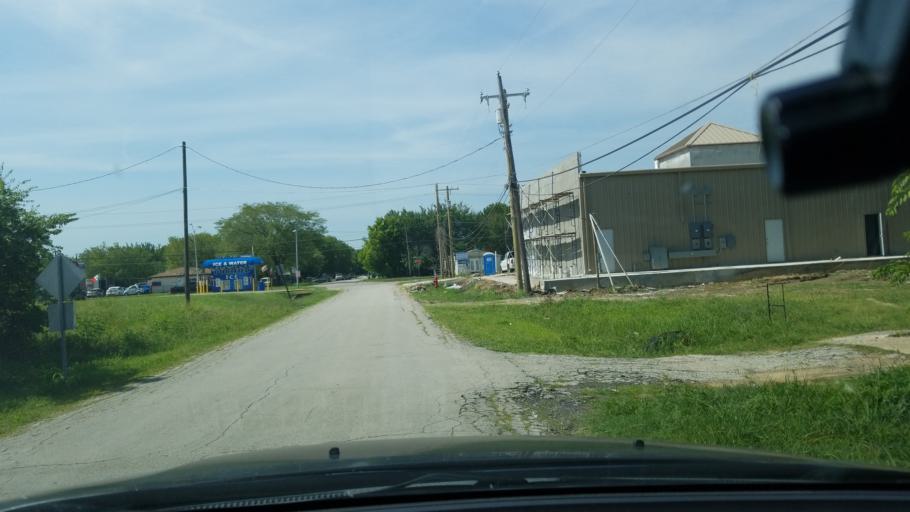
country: US
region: Texas
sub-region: Dallas County
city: Balch Springs
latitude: 32.7350
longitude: -96.6265
